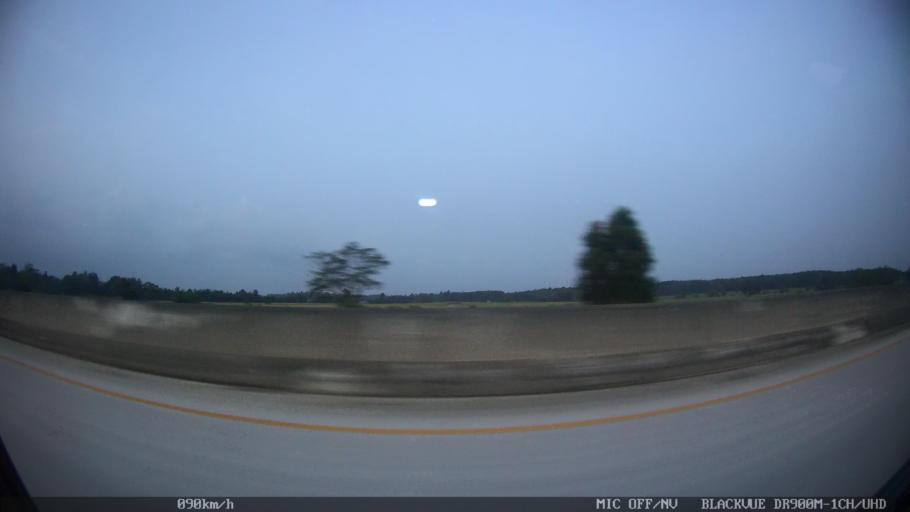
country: ID
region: Lampung
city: Sidorejo
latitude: -5.5764
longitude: 105.5408
